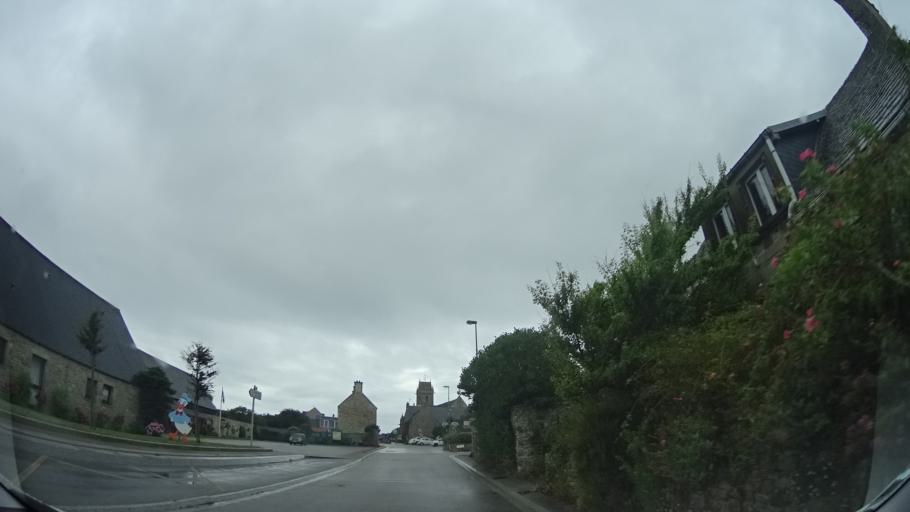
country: FR
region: Lower Normandy
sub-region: Departement de la Manche
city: Beaumont-Hague
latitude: 49.6134
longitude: -1.8210
